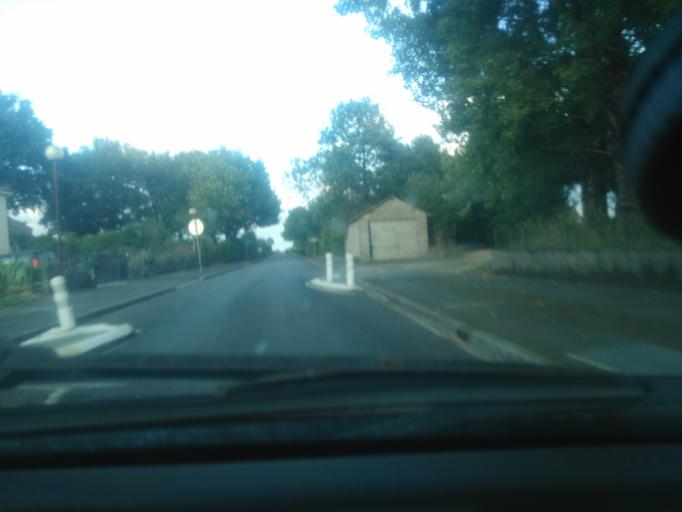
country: FR
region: Pays de la Loire
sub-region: Departement de la Vendee
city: La Ferriere
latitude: 46.7125
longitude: -1.3046
